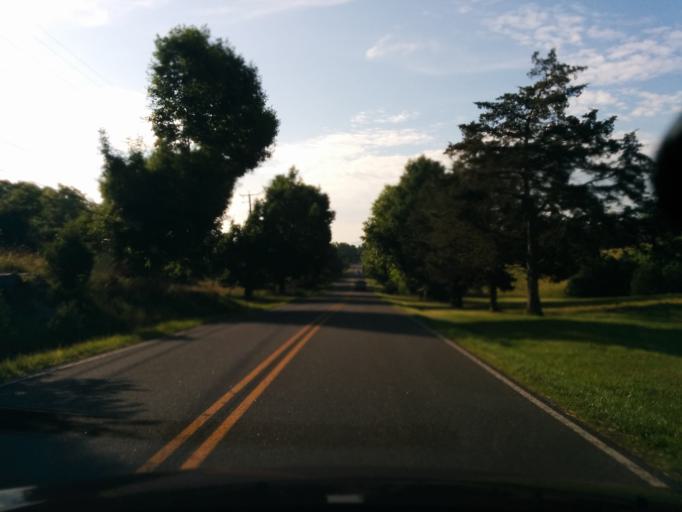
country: US
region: Virginia
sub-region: City of Lexington
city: Lexington
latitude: 37.8014
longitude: -79.4638
